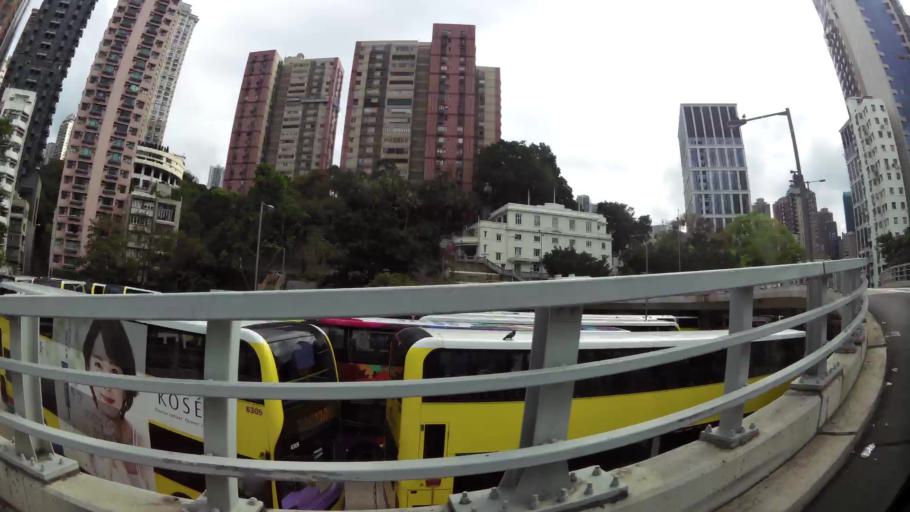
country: HK
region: Wanchai
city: Wan Chai
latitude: 22.2790
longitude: 114.1903
